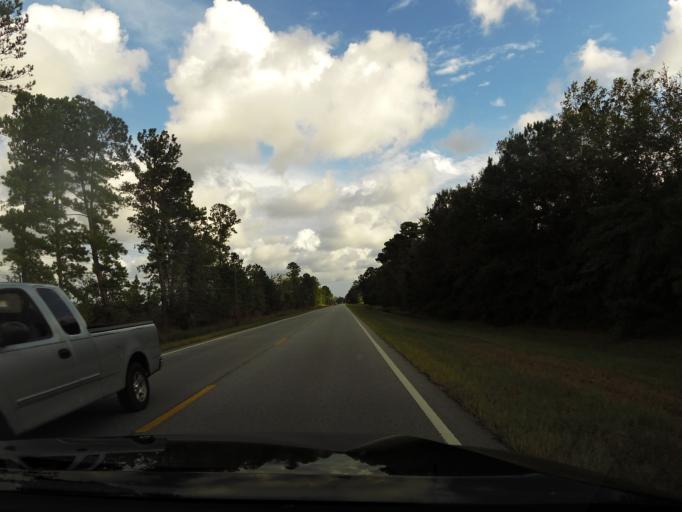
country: US
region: Georgia
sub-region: Liberty County
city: Midway
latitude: 31.7638
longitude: -81.4475
